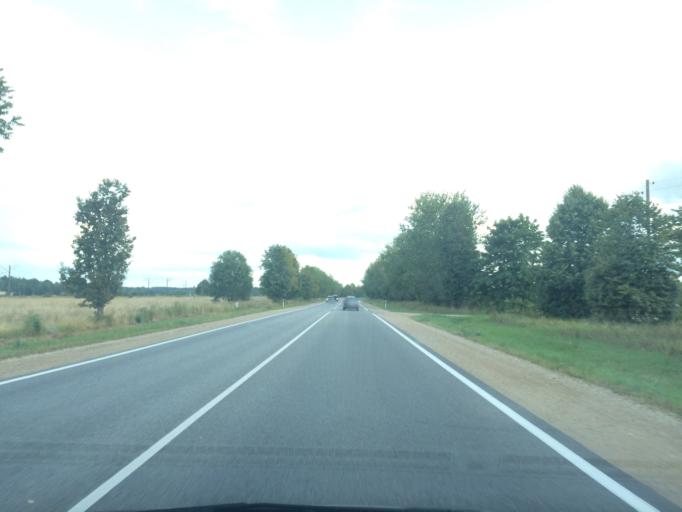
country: LV
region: Ogre
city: Ogre
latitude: 56.7915
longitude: 24.6350
